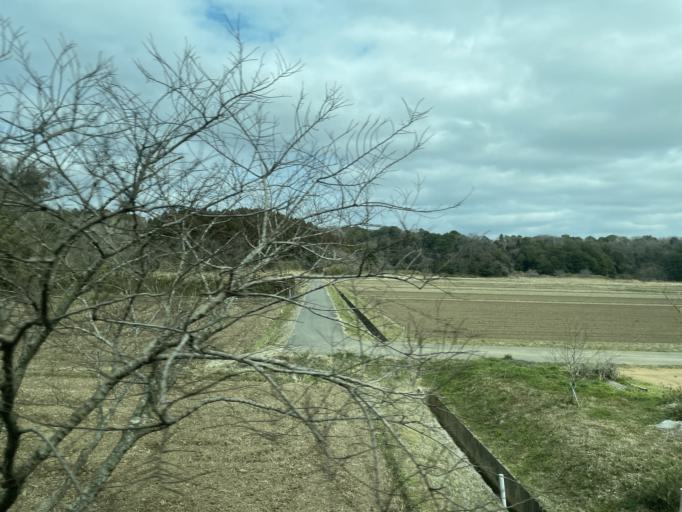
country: JP
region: Chiba
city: Narita
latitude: 35.8189
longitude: 140.2673
